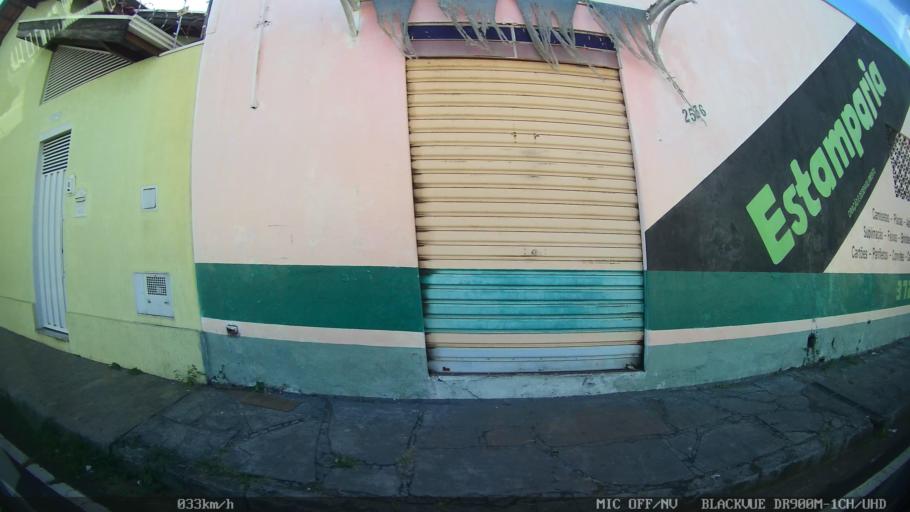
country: BR
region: Sao Paulo
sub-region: Franca
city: Franca
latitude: -20.5315
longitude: -47.3997
